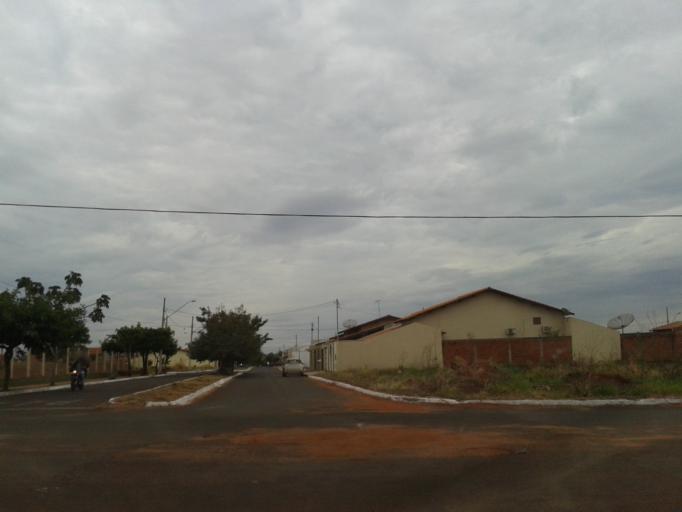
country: BR
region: Minas Gerais
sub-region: Santa Vitoria
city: Santa Vitoria
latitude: -18.8534
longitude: -50.1225
